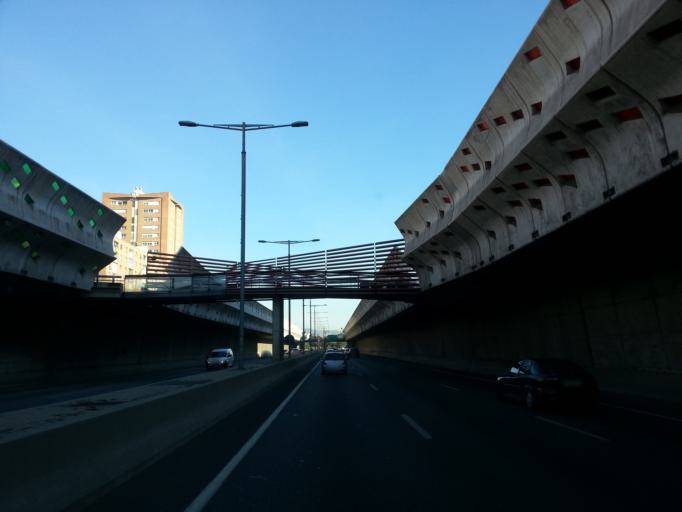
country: ES
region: Catalonia
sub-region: Provincia de Barcelona
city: Sant Marti
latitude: 41.4202
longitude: 2.2094
